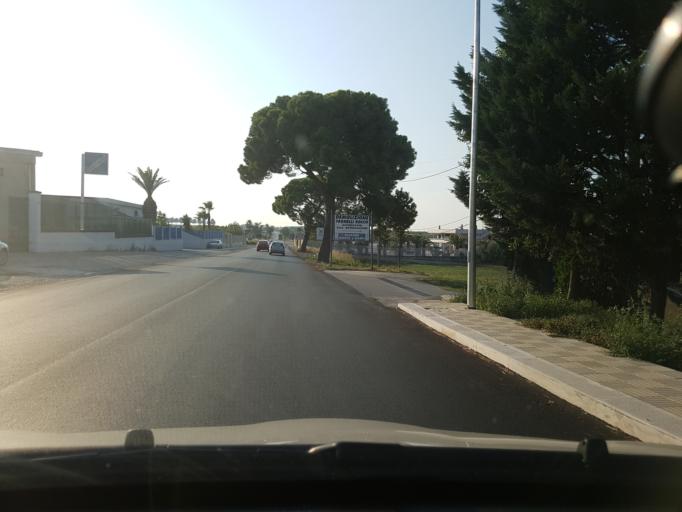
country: IT
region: Apulia
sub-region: Provincia di Foggia
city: Cerignola
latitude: 41.2681
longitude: 15.8840
